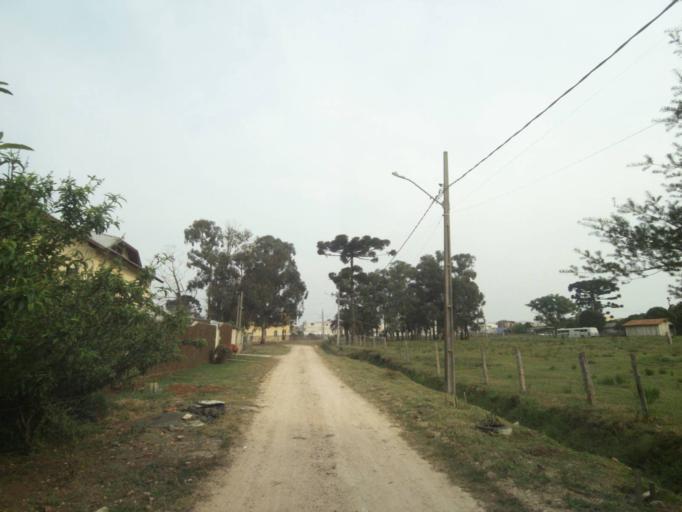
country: BR
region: Parana
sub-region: Sao Jose Dos Pinhais
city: Sao Jose dos Pinhais
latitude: -25.5252
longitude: -49.2772
